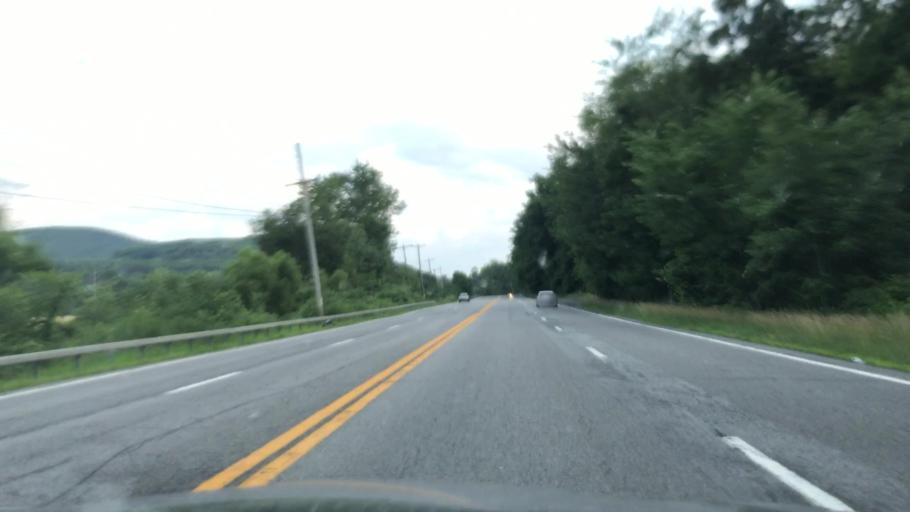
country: US
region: New York
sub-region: Orange County
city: Harriman
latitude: 41.2842
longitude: -74.1466
